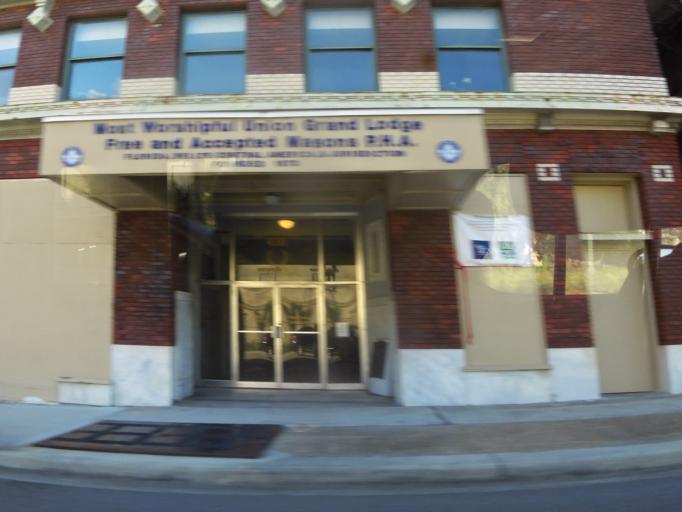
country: US
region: Florida
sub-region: Duval County
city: Jacksonville
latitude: 30.3311
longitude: -81.6644
